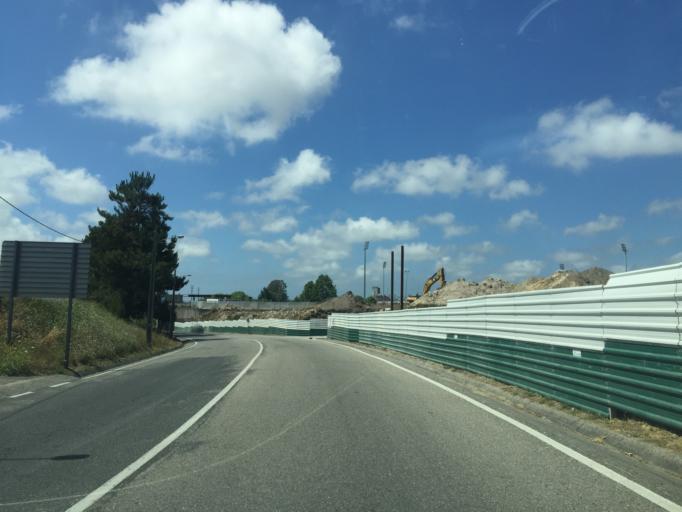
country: PT
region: Leiria
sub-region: Marinha Grande
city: Marinha Grande
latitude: 39.7331
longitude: -8.9300
